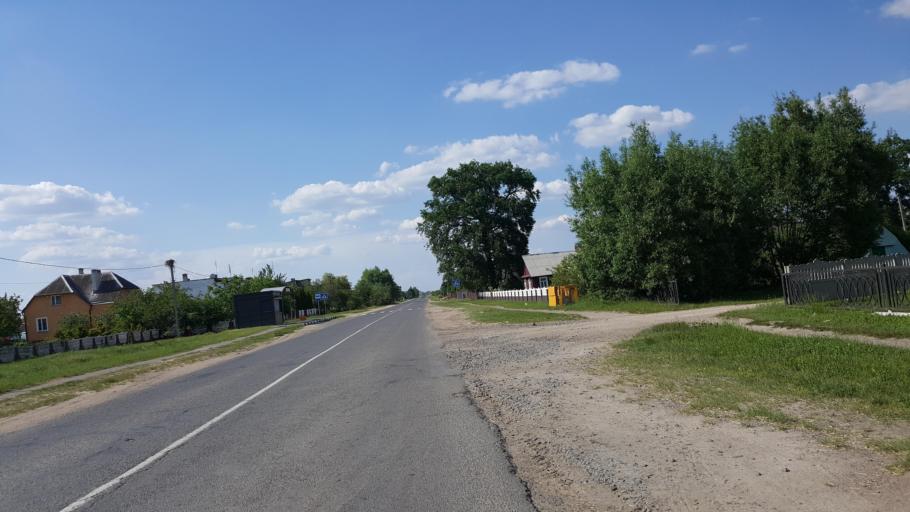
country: BY
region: Brest
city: Kobryn
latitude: 52.3009
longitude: 24.2754
